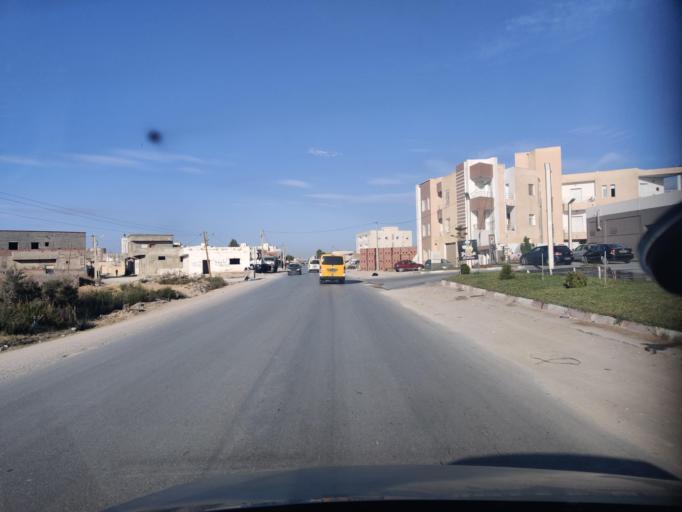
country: TN
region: Ariana
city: Ariana
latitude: 36.9562
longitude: 10.2223
